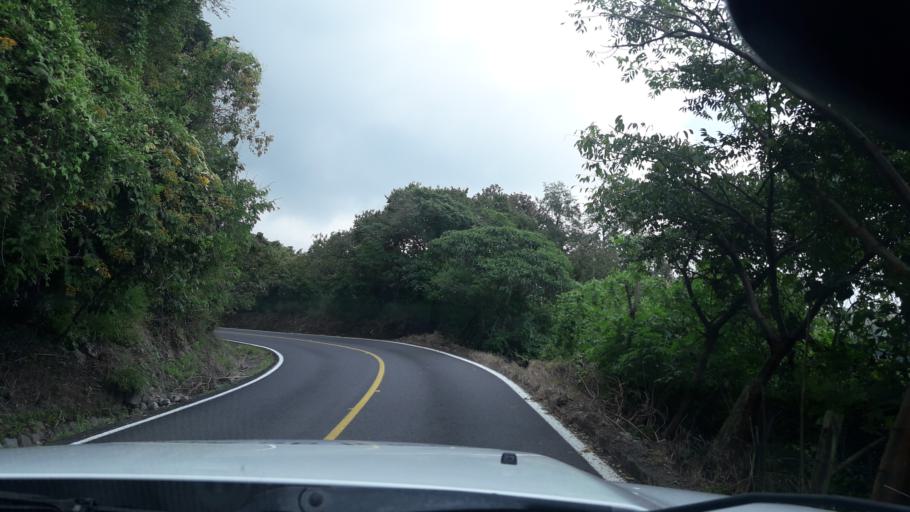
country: MX
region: Colima
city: Suchitlan
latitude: 19.4337
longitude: -103.7134
